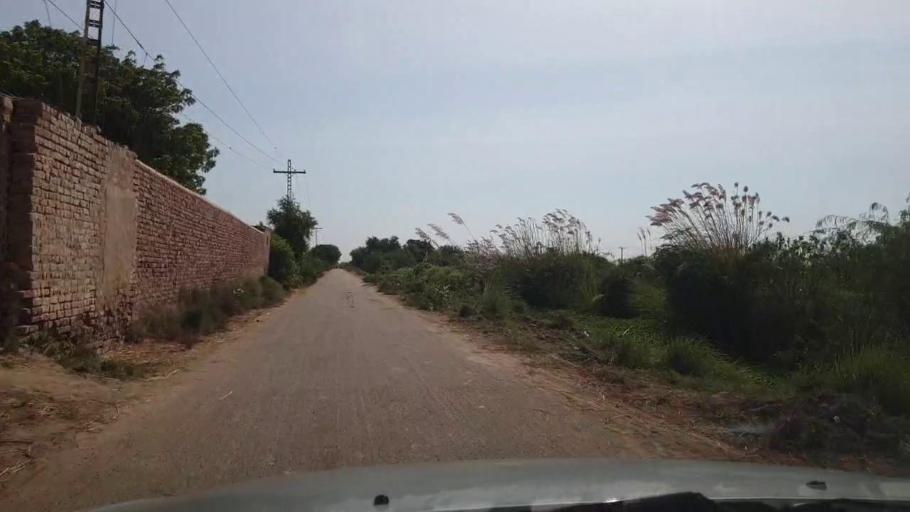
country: PK
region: Sindh
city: Tando Muhammad Khan
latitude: 25.1508
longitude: 68.3891
